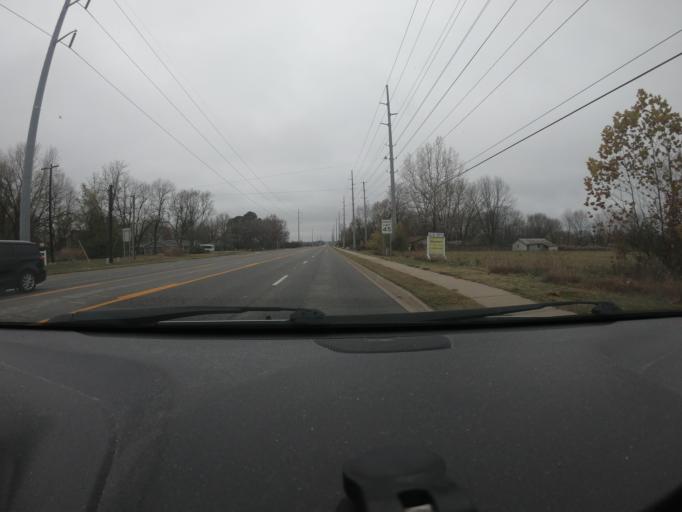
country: US
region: Arkansas
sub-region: Benton County
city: Bentonville
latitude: 36.3576
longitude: -94.2327
